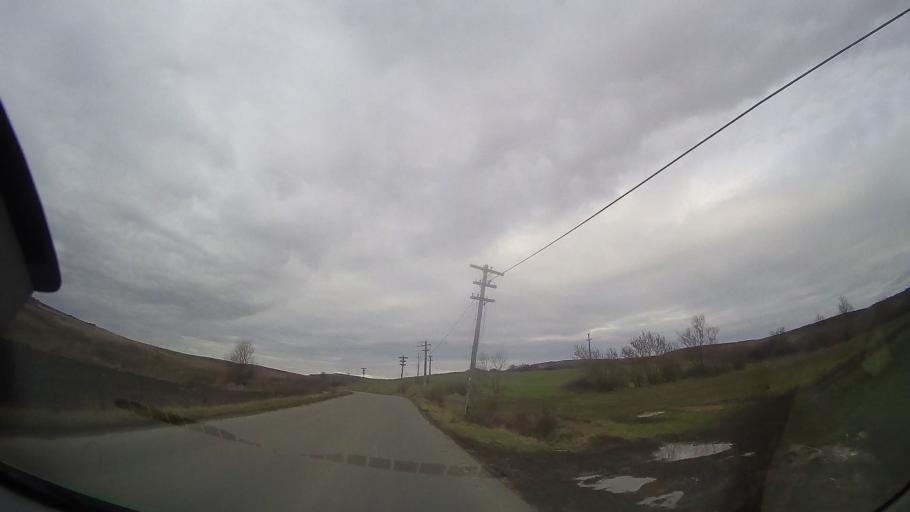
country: RO
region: Mures
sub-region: Comuna Faragau
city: Faragau
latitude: 46.7429
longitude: 24.5360
